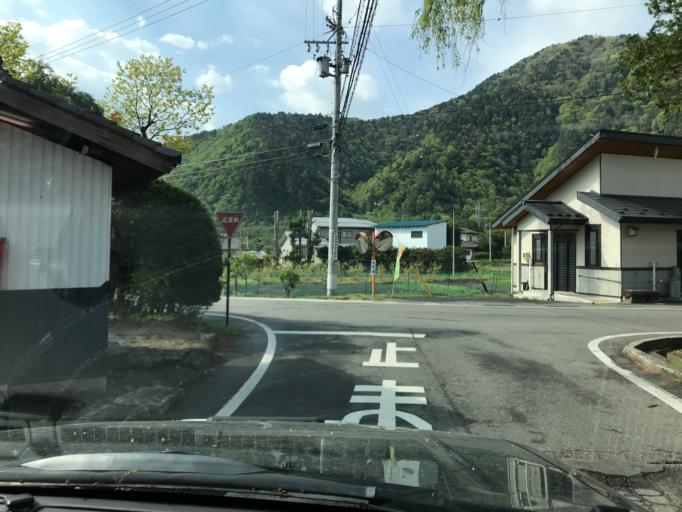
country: JP
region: Nagano
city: Omachi
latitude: 36.5147
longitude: 137.8143
